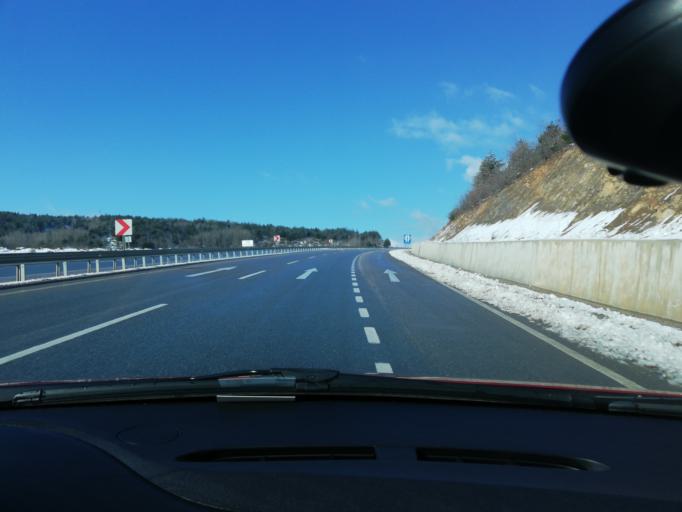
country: TR
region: Kastamonu
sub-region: Cide
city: Kastamonu
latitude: 41.3598
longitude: 33.6902
